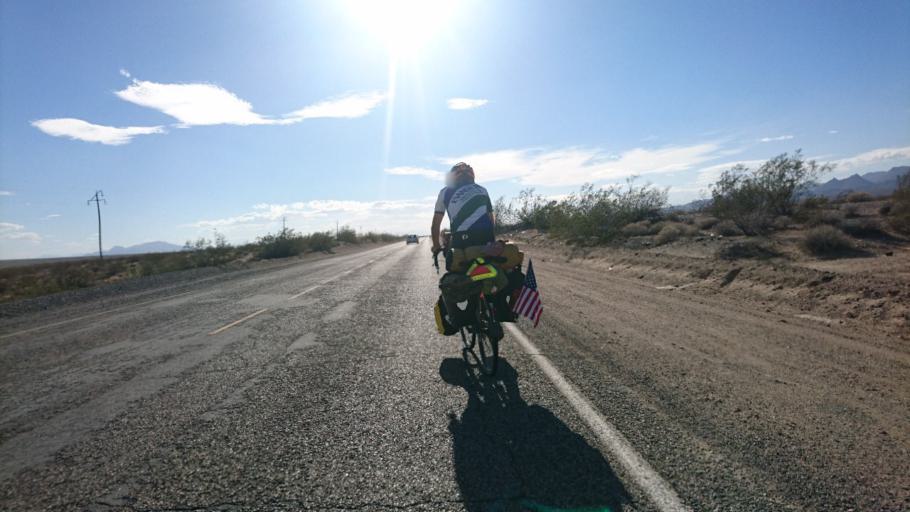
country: US
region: California
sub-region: San Bernardino County
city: Needles
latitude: 34.7180
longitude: -115.2732
